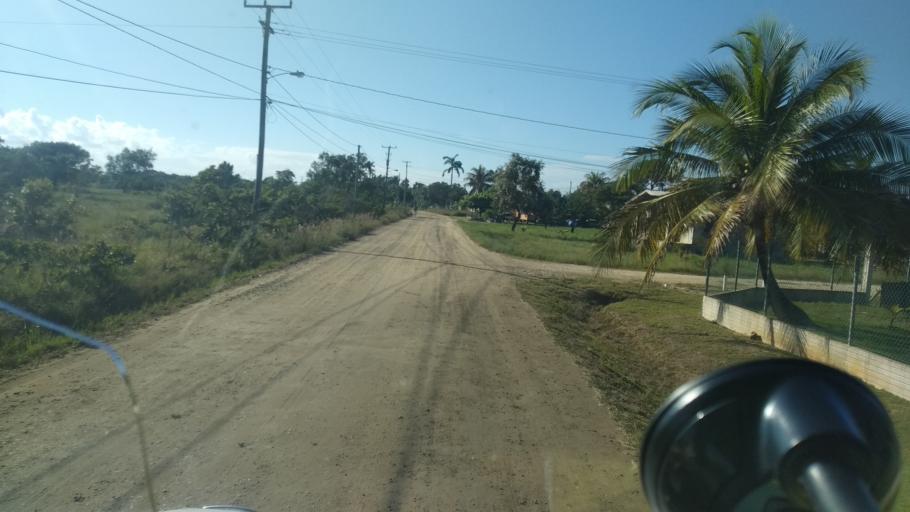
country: BZ
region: Belize
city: Belize City
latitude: 17.5595
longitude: -88.3274
